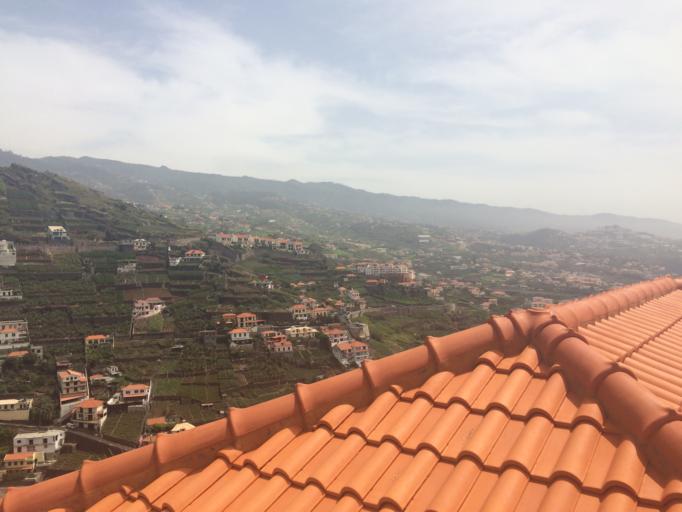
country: PT
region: Madeira
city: Camara de Lobos
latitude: 32.6553
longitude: -16.9915
